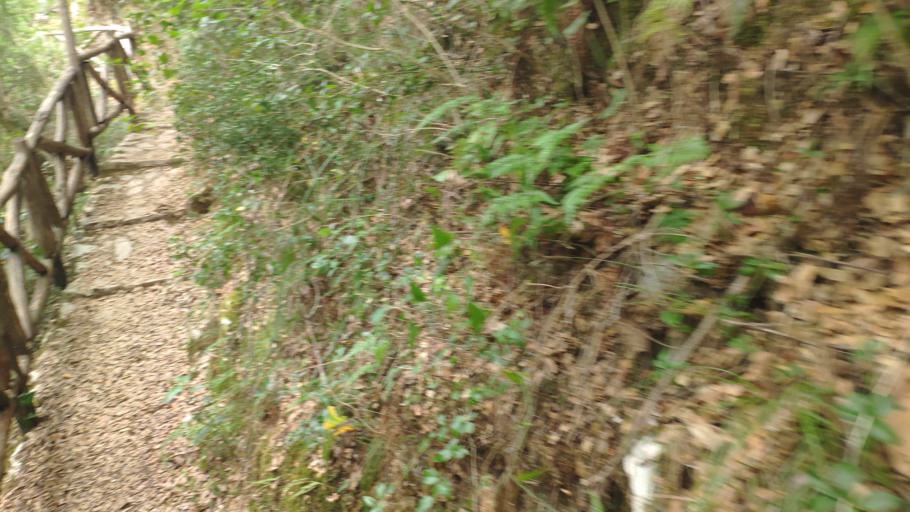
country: GR
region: Ionian Islands
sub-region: Lefkada
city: Lefkada
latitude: 38.8035
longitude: 20.6744
